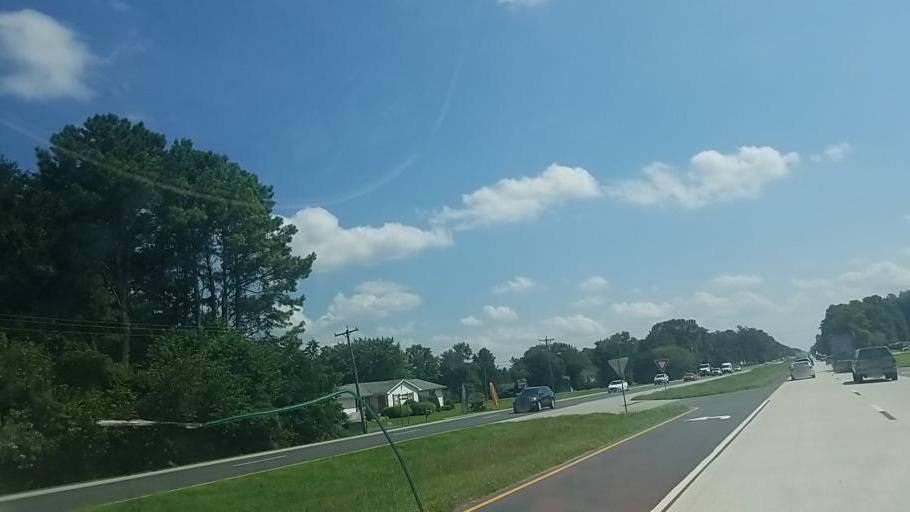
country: US
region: Delaware
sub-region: Sussex County
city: Milford
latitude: 38.8511
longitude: -75.4393
